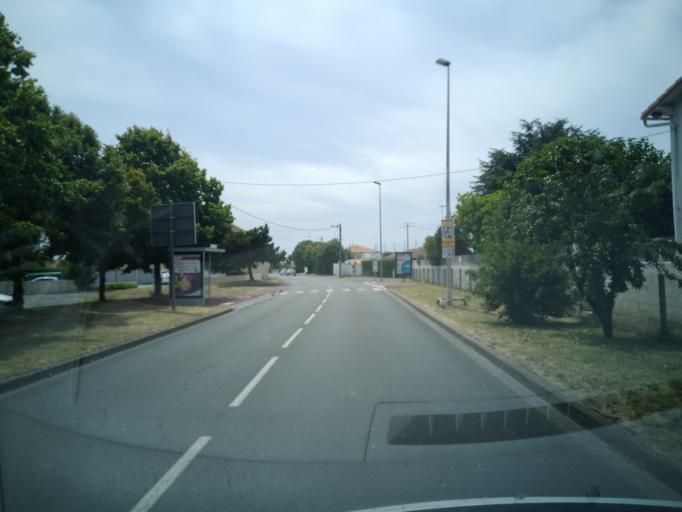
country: FR
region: Poitou-Charentes
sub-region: Departement de la Charente-Maritime
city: Saint-Palais-sur-Mer
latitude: 45.6521
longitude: -1.0798
